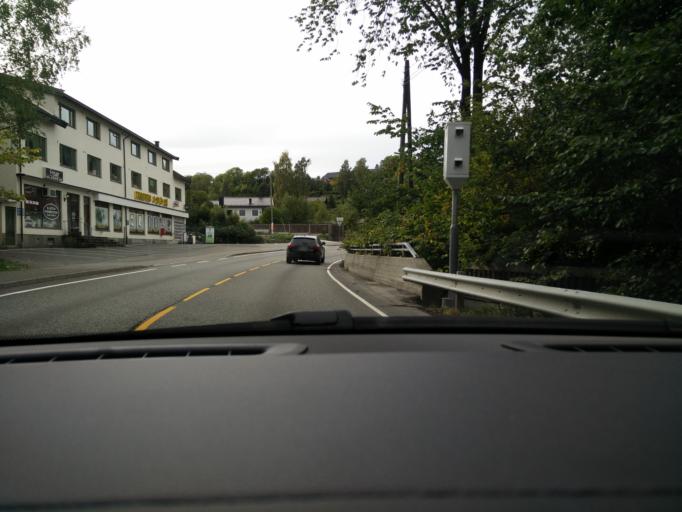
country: NO
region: Akershus
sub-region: Asker
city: Blakstad
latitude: 59.8153
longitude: 10.4681
